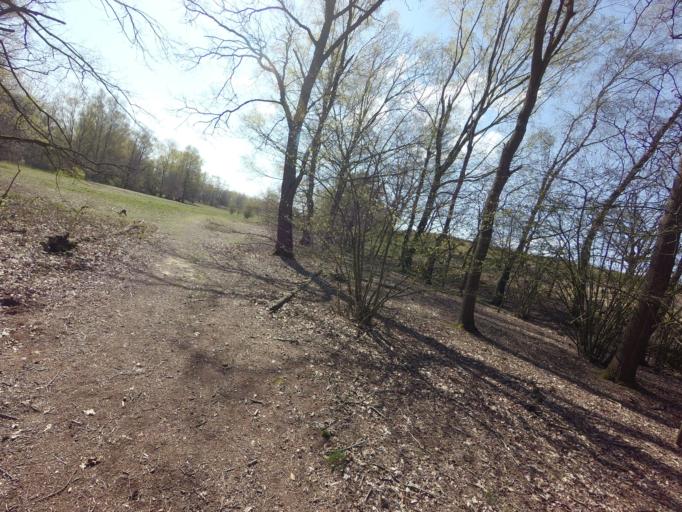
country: NL
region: Limburg
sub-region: Gemeente Bergen
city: Wellerlooi
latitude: 51.6082
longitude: 6.0717
